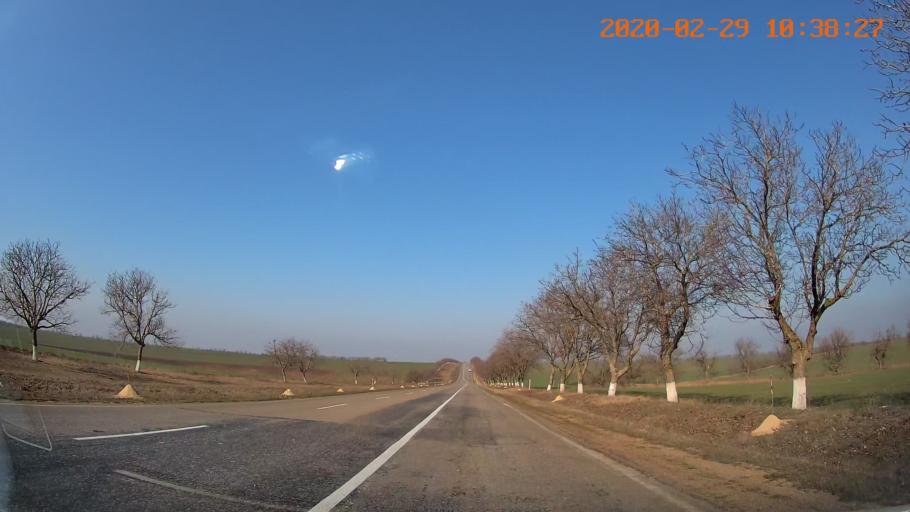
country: MD
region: Anenii Noi
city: Varnita
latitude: 47.0161
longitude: 29.4728
